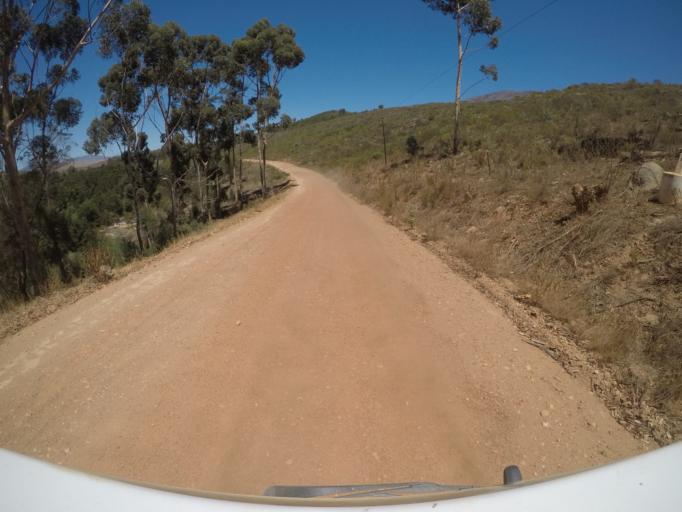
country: ZA
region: Western Cape
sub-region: Overberg District Municipality
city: Caledon
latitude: -34.1817
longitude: 19.2232
